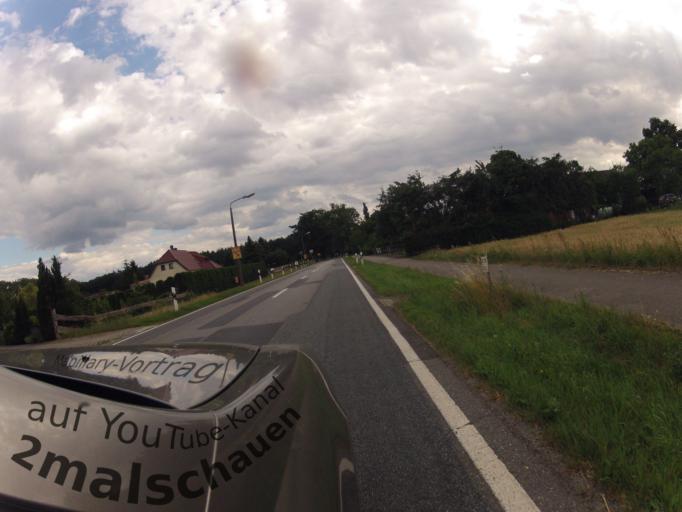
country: DE
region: Mecklenburg-Vorpommern
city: Lassan
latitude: 53.8982
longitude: 13.7864
